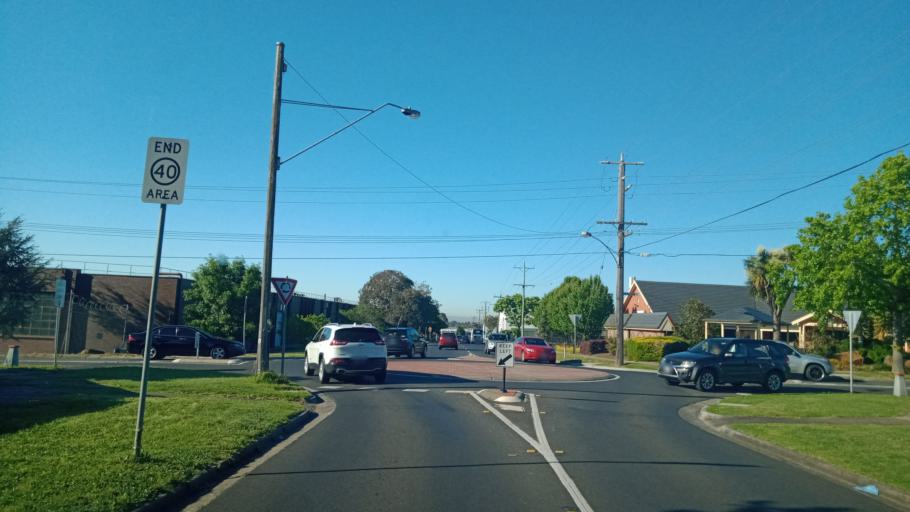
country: AU
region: Victoria
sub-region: Greater Dandenong
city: Springvale
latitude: -37.9387
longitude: 145.1710
